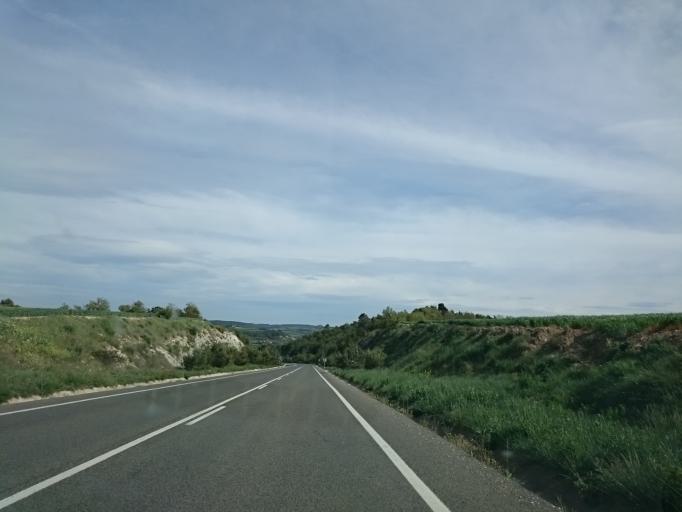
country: ES
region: Catalonia
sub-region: Provincia de Tarragona
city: Santa Coloma de Queralt
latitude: 41.5612
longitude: 1.3989
